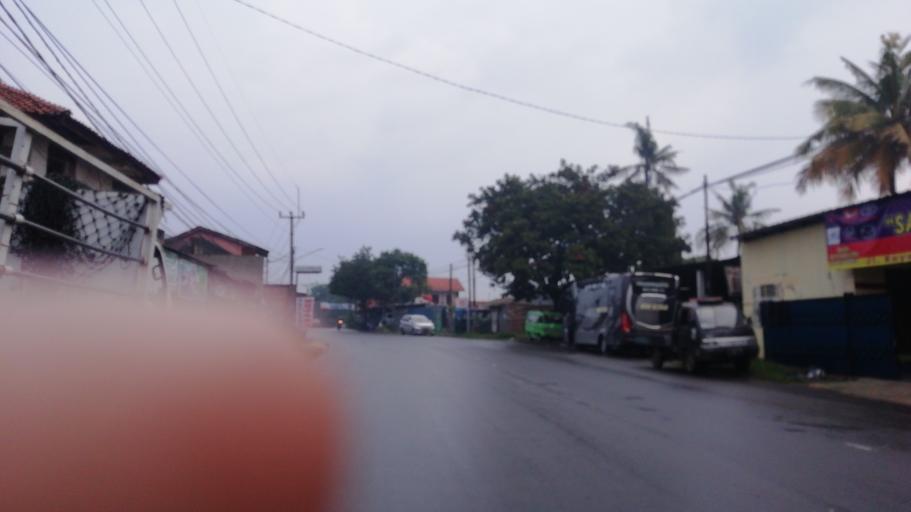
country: ID
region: West Java
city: Bogor
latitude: -6.5404
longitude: 106.8060
